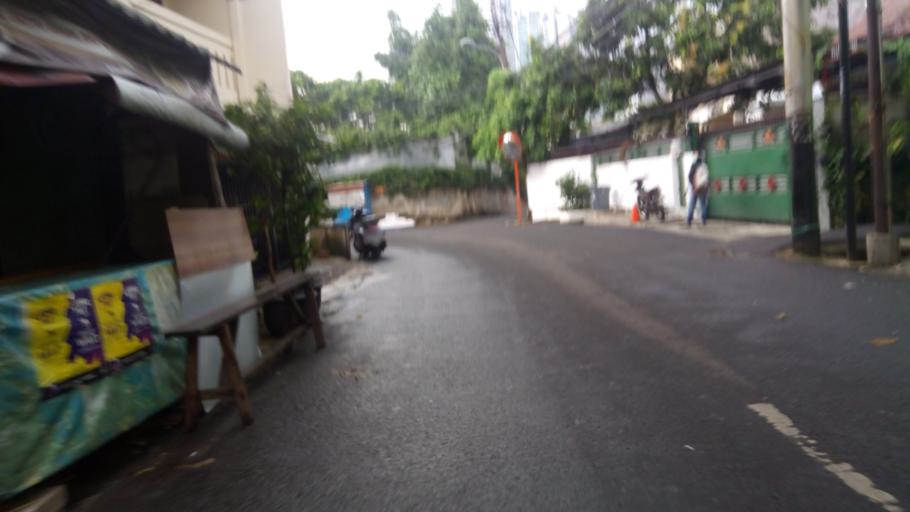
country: ID
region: Jakarta Raya
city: Jakarta
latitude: -6.2597
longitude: 106.8063
